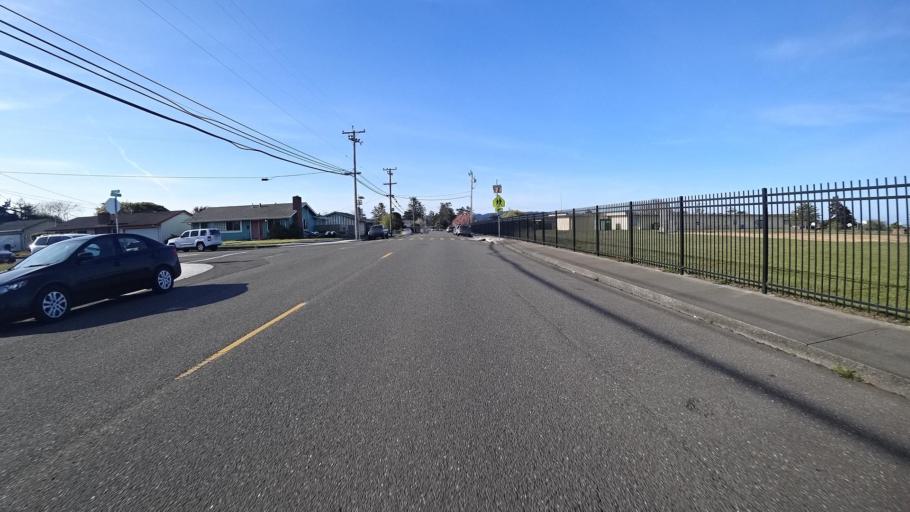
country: US
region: California
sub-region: Humboldt County
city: Bayview
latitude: 40.7593
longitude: -124.1810
